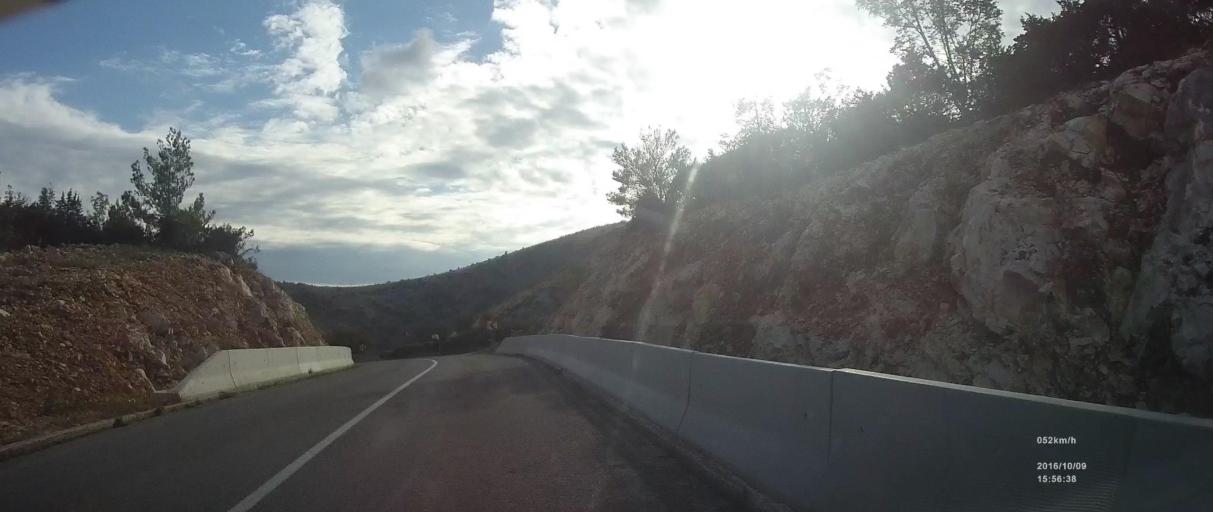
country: HR
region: Splitsko-Dalmatinska
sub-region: Grad Trogir
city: Trogir
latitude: 43.5771
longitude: 16.2327
